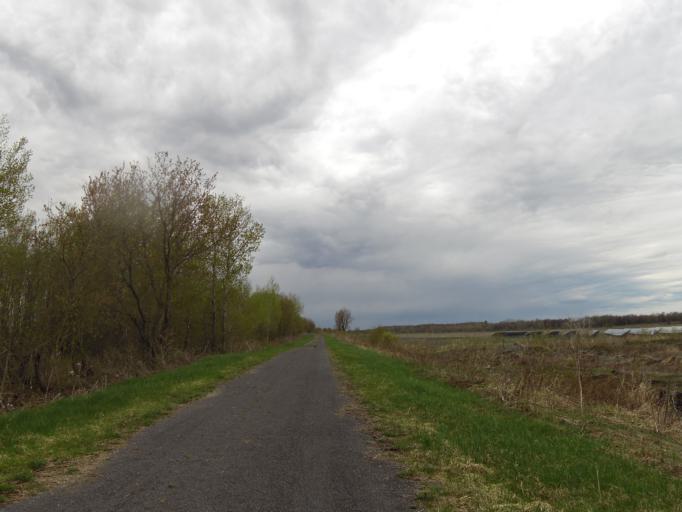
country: CA
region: Quebec
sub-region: Outaouais
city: Papineauville
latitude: 45.5328
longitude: -74.8856
